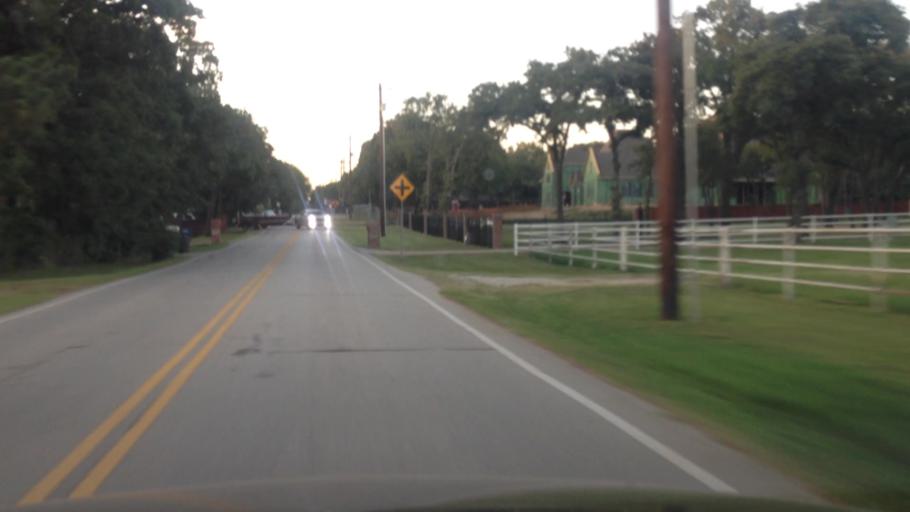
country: US
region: Texas
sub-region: Tarrant County
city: Keller
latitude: 32.9472
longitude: -97.2031
